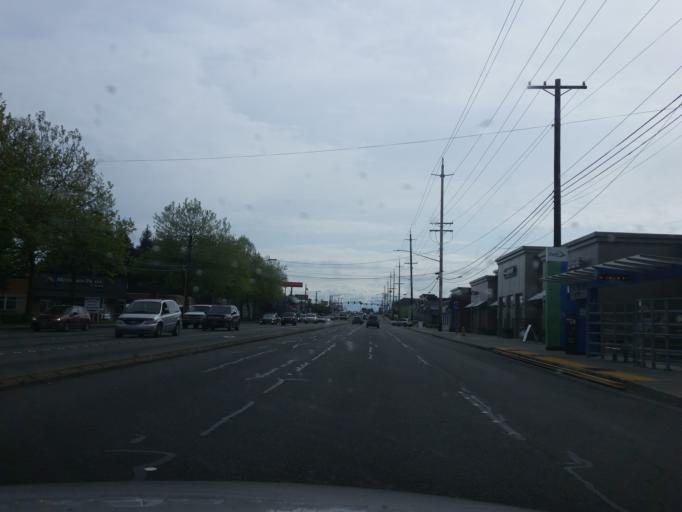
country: US
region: Washington
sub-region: Snohomish County
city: Lynnwood
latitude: 47.8208
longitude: -122.3154
